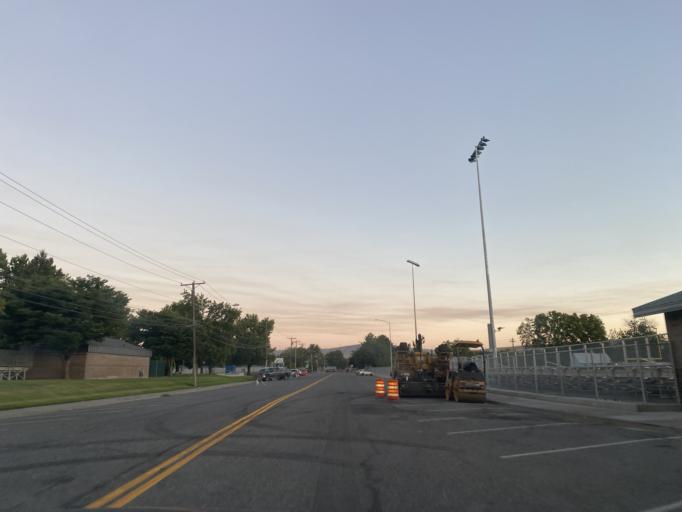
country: US
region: Washington
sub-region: Benton County
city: Kennewick
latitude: 46.2023
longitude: -119.1230
